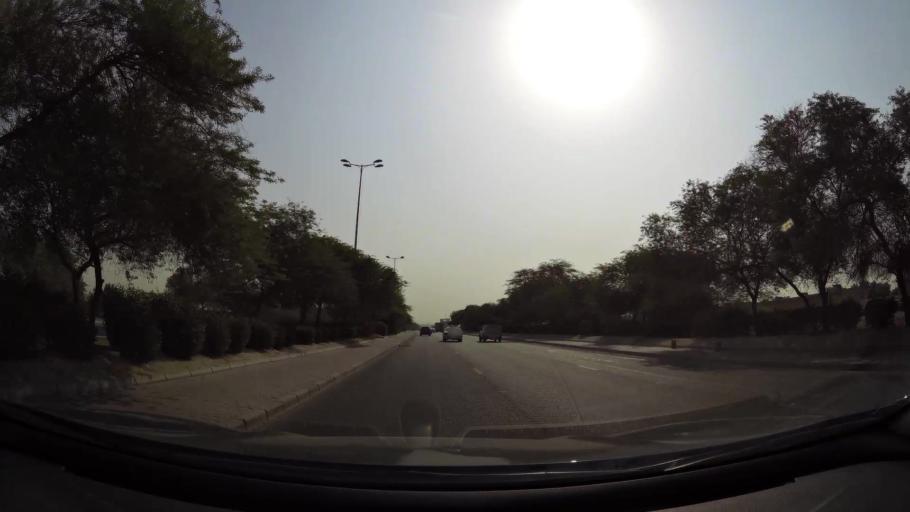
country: KW
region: Al Asimah
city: Ar Rabiyah
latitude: 29.2770
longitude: 47.8451
